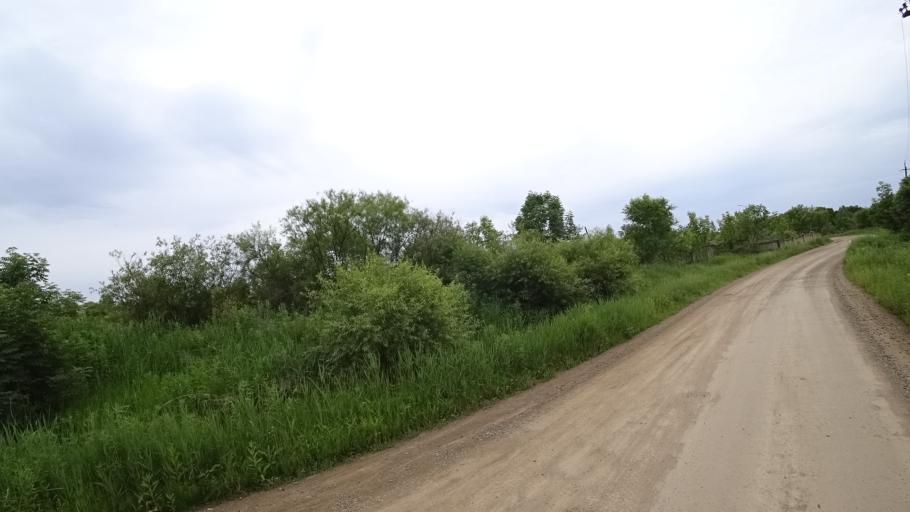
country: RU
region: Primorskiy
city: Arsen'yev
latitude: 44.1980
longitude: 133.3084
